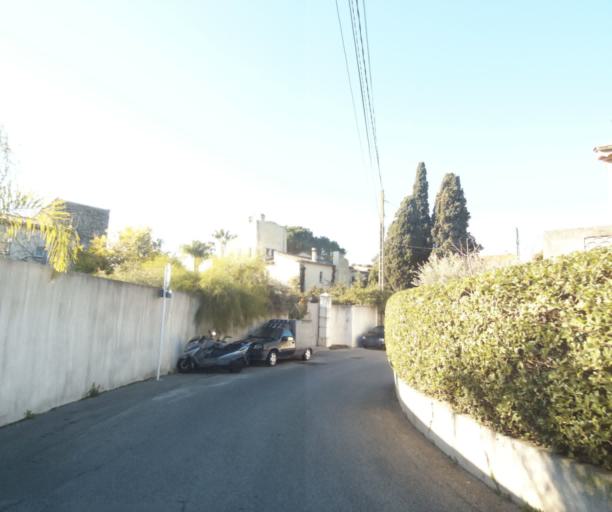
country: FR
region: Provence-Alpes-Cote d'Azur
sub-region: Departement des Alpes-Maritimes
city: Antibes
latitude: 43.5794
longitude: 7.1004
